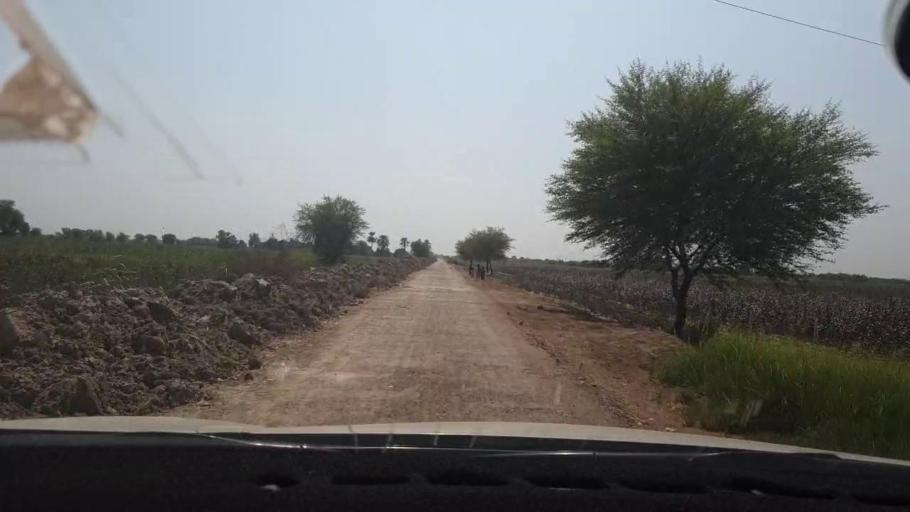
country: PK
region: Sindh
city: Tando Mittha Khan
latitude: 25.9021
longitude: 69.2066
